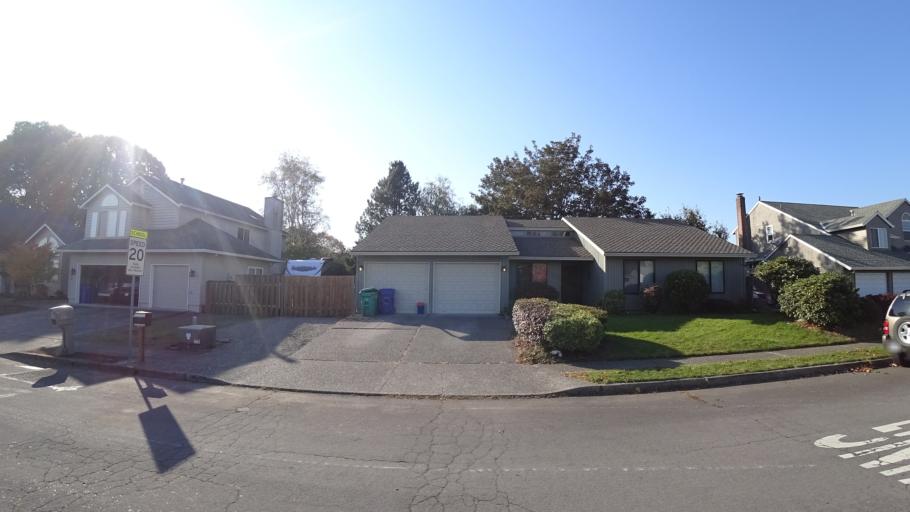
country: US
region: Oregon
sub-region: Multnomah County
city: Gresham
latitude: 45.5144
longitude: -122.4264
